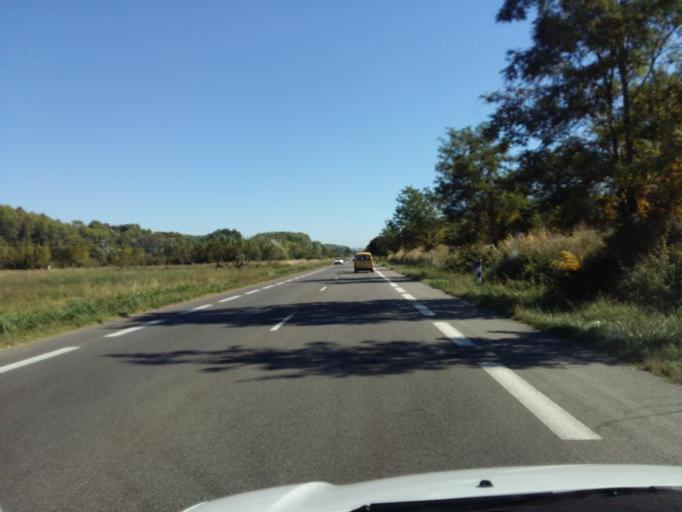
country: FR
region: Provence-Alpes-Cote d'Azur
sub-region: Departement des Bouches-du-Rhone
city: Charleval
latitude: 43.7528
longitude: 5.2523
